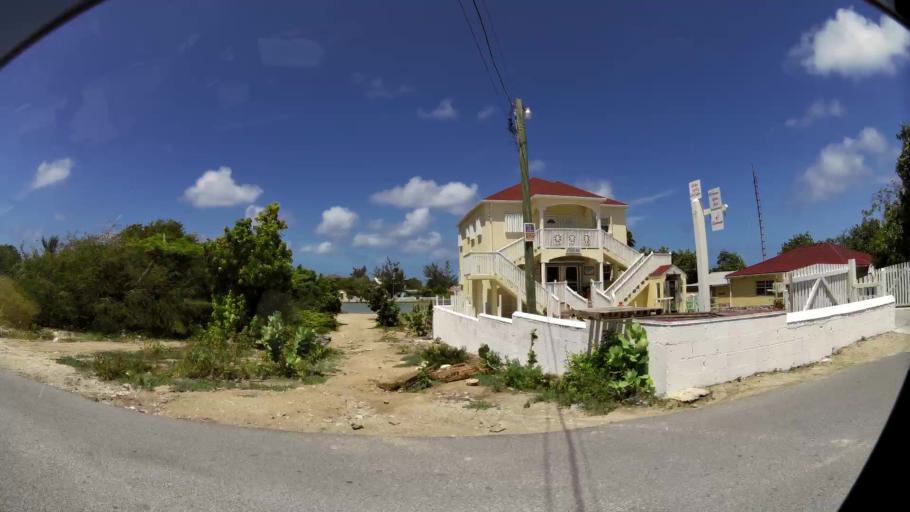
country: TC
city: Cockburn Town
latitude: 21.4743
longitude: -71.1462
